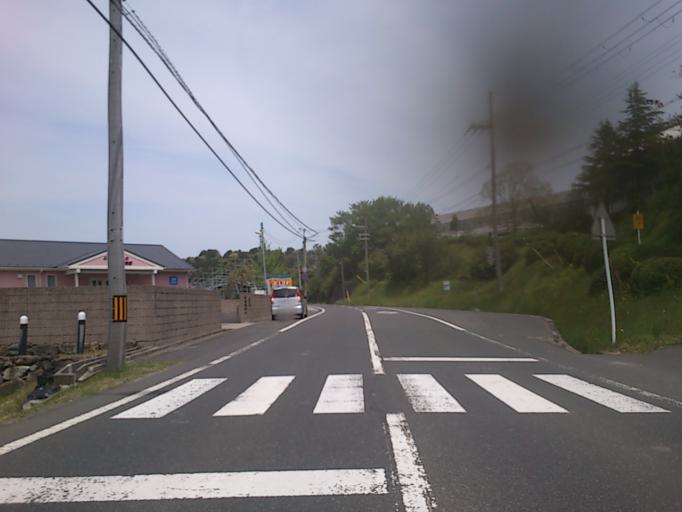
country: JP
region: Kyoto
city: Miyazu
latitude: 35.6718
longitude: 135.0935
